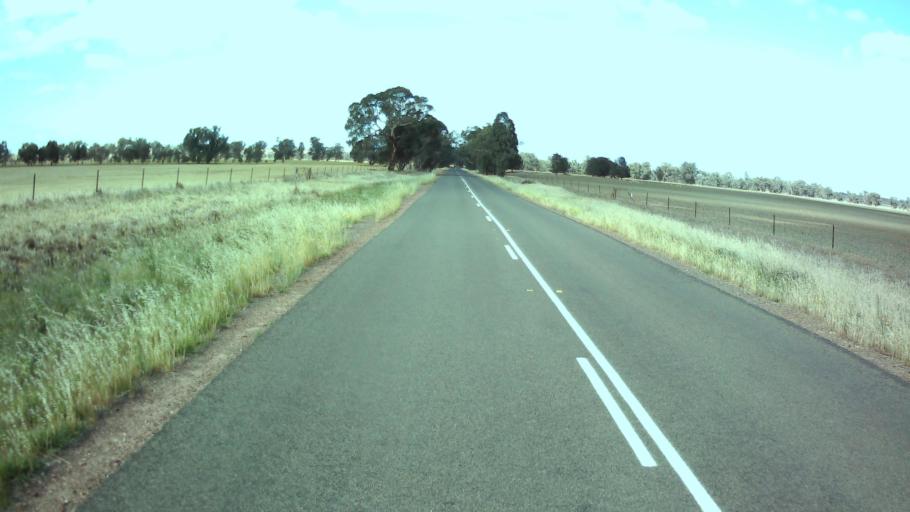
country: AU
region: New South Wales
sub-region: Weddin
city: Grenfell
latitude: -33.9798
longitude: 148.4194
